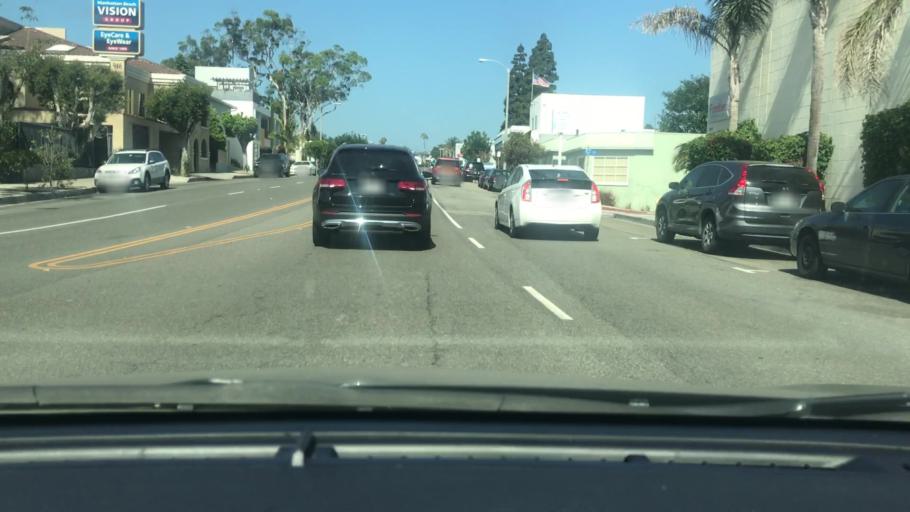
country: US
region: California
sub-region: Los Angeles County
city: Manhattan Beach
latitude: 33.8874
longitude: -118.3983
